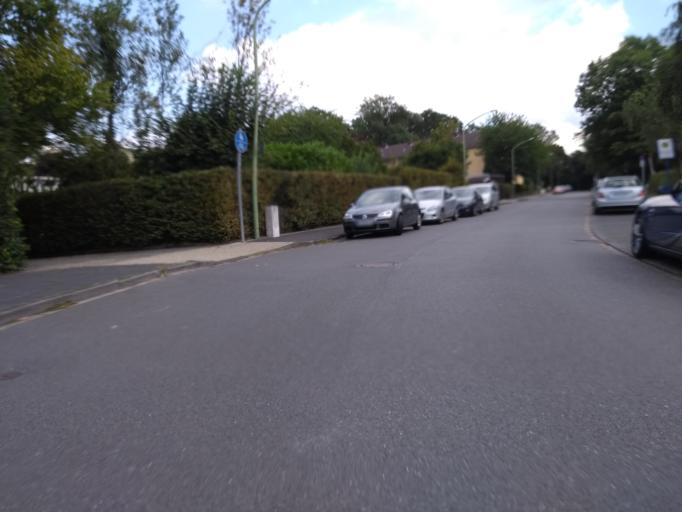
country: DE
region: North Rhine-Westphalia
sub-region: Regierungsbezirk Arnsberg
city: Hagen
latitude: 51.3970
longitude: 7.4728
